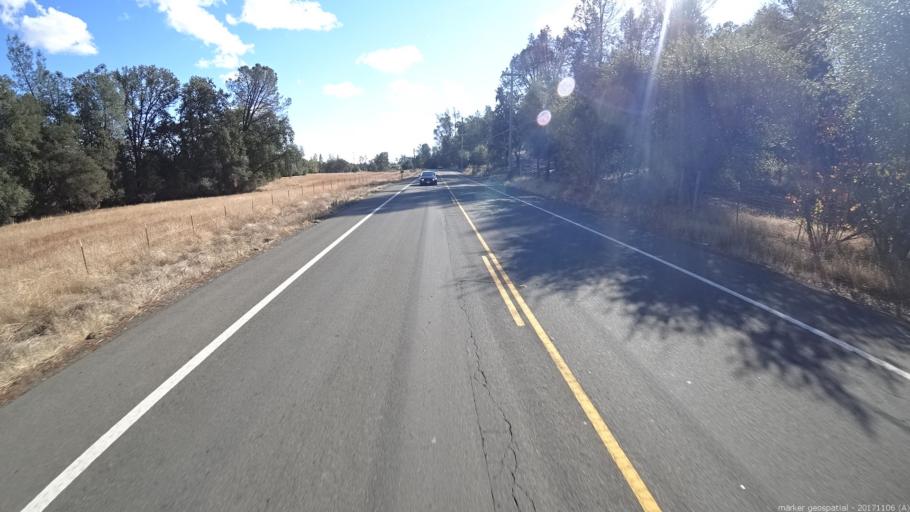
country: US
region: California
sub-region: Shasta County
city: Palo Cedro
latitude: 40.5916
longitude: -122.3087
